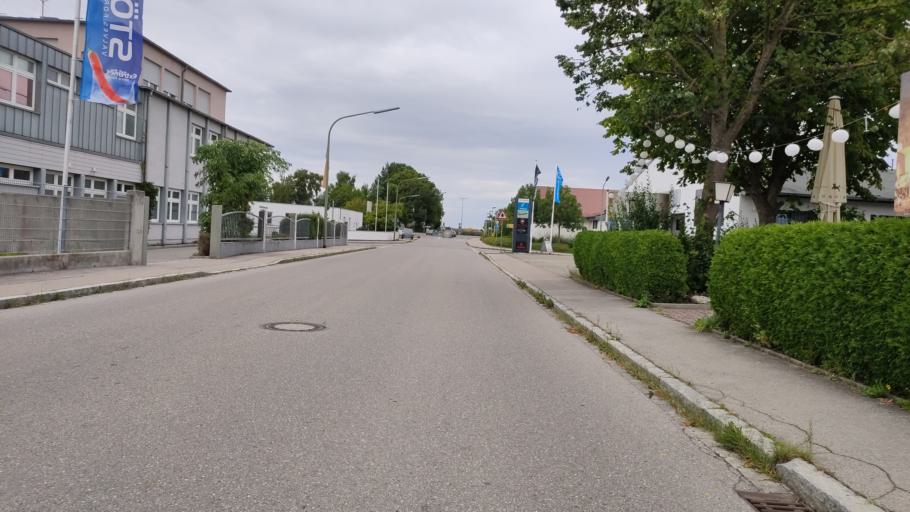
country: DE
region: Bavaria
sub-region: Swabia
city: Konigsbrunn
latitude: 48.2552
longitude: 10.8730
